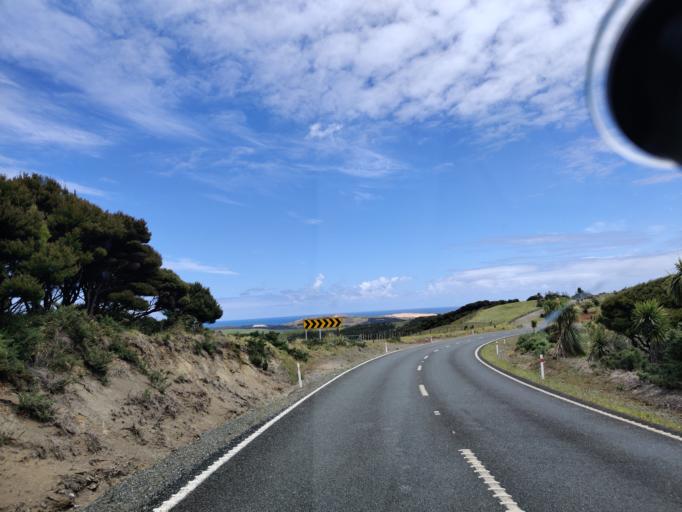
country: NZ
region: Northland
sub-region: Far North District
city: Ahipara
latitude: -34.4884
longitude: 172.7581
